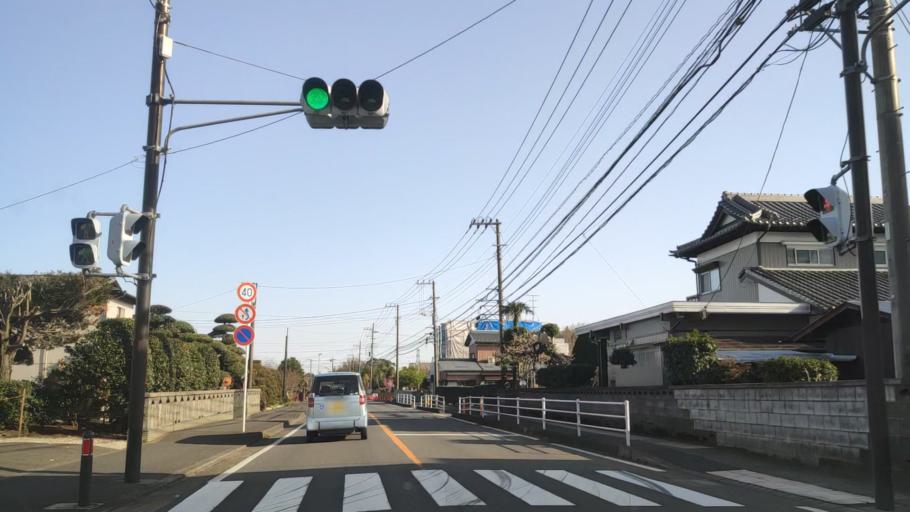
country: JP
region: Kanagawa
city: Zama
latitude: 35.5282
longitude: 139.3215
